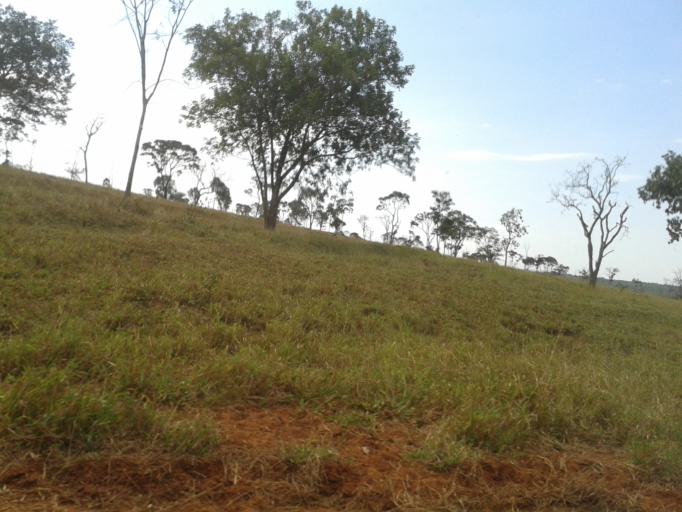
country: BR
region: Minas Gerais
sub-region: Ituiutaba
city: Ituiutaba
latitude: -19.0747
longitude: -49.3635
